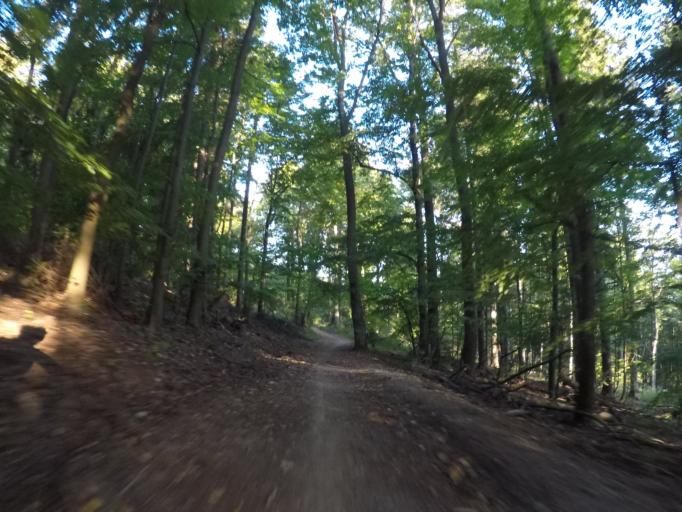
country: SK
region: Kosicky
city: Kosice
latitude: 48.7489
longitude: 21.1891
